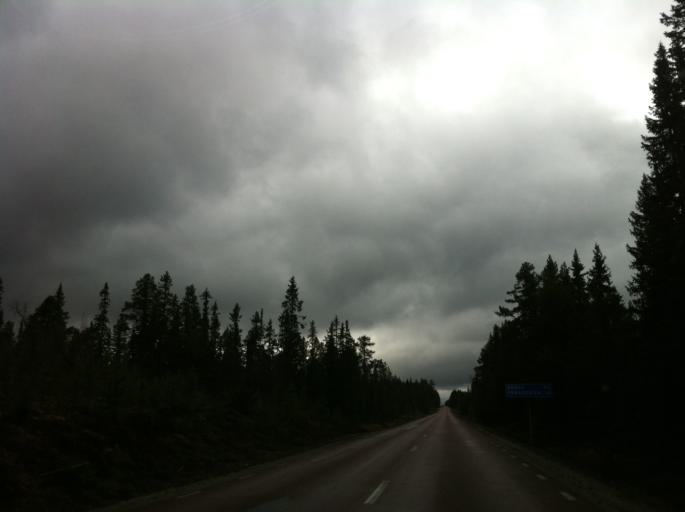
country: NO
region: Hedmark
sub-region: Engerdal
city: Engerdal
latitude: 62.4366
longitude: 12.7136
